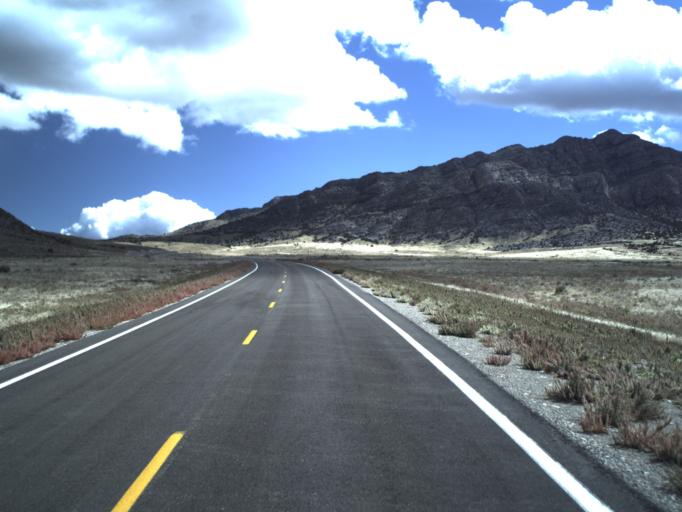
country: US
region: Utah
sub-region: Beaver County
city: Milford
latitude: 38.5062
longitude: -113.6100
